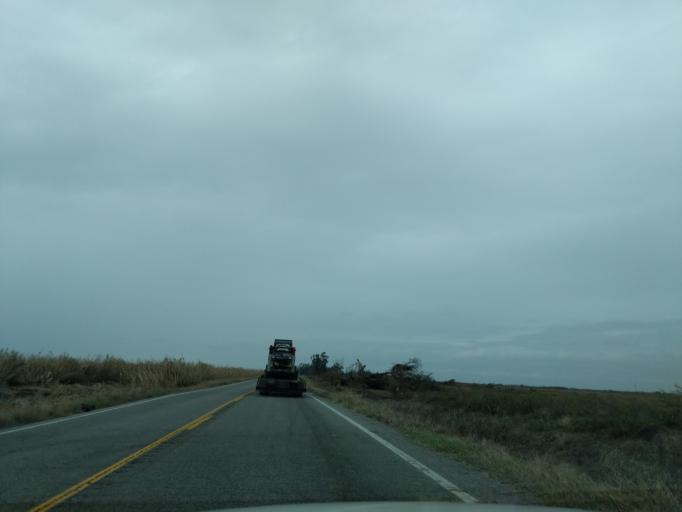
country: US
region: Louisiana
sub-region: Cameron Parish
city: Cameron
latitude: 29.7796
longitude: -93.0584
